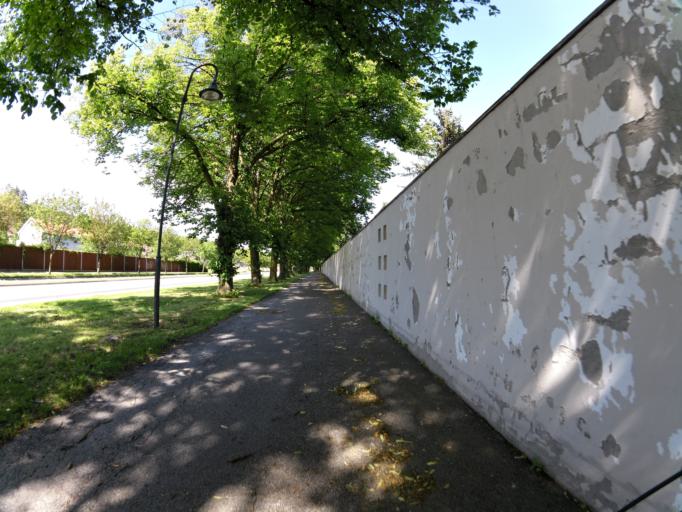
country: NO
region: Ostfold
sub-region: Fredrikstad
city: Fredrikstad
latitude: 59.2264
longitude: 10.9546
